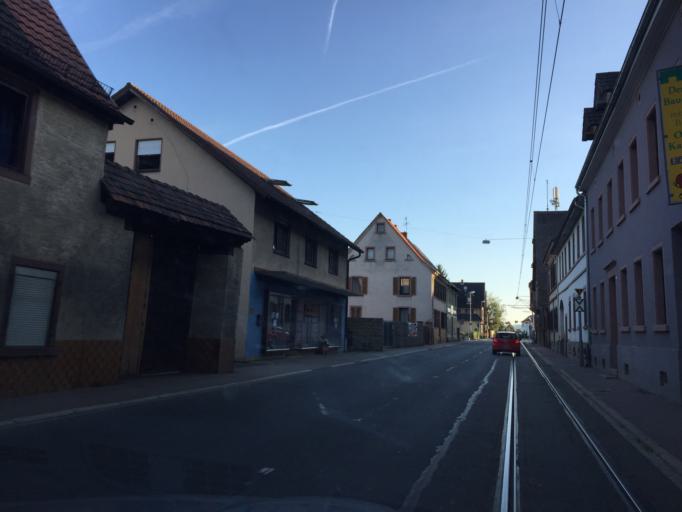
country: DE
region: Baden-Wuerttemberg
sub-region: Karlsruhe Region
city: Weinheim
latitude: 49.5126
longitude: 8.6563
